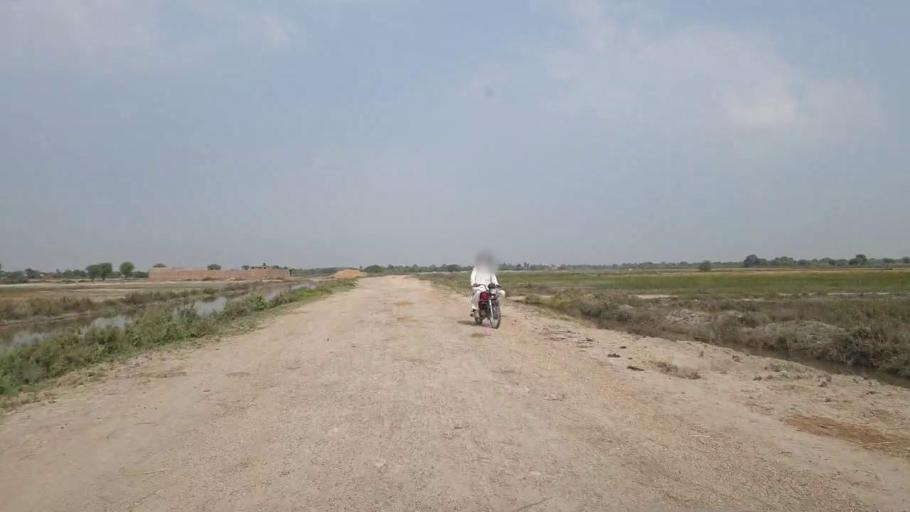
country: PK
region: Sindh
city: Matli
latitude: 24.9678
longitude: 68.6933
